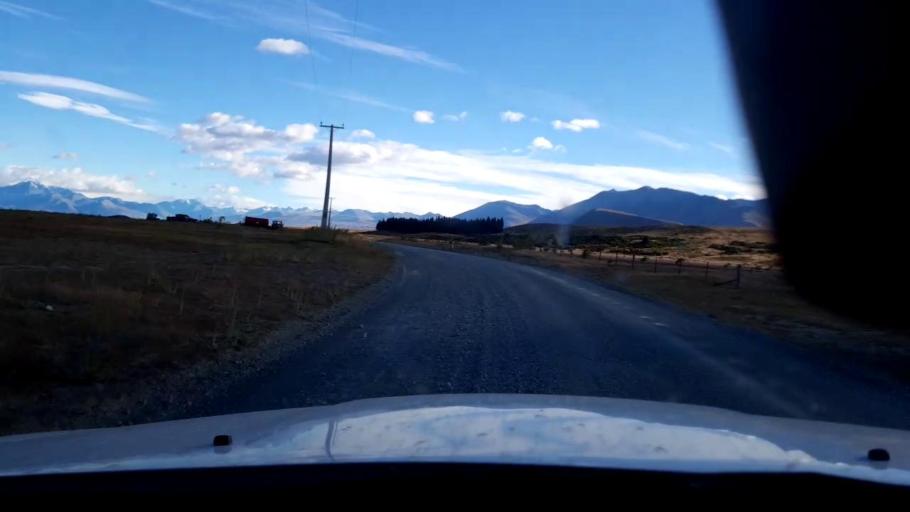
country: NZ
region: Canterbury
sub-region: Timaru District
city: Pleasant Point
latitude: -43.9917
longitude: 170.5017
